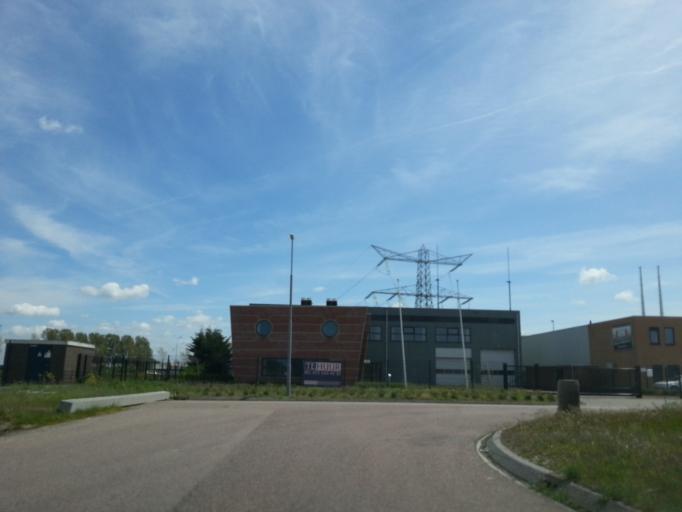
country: NL
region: North Holland
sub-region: Gemeente Beverwijk
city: Beverwijk
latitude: 52.4747
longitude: 4.6787
